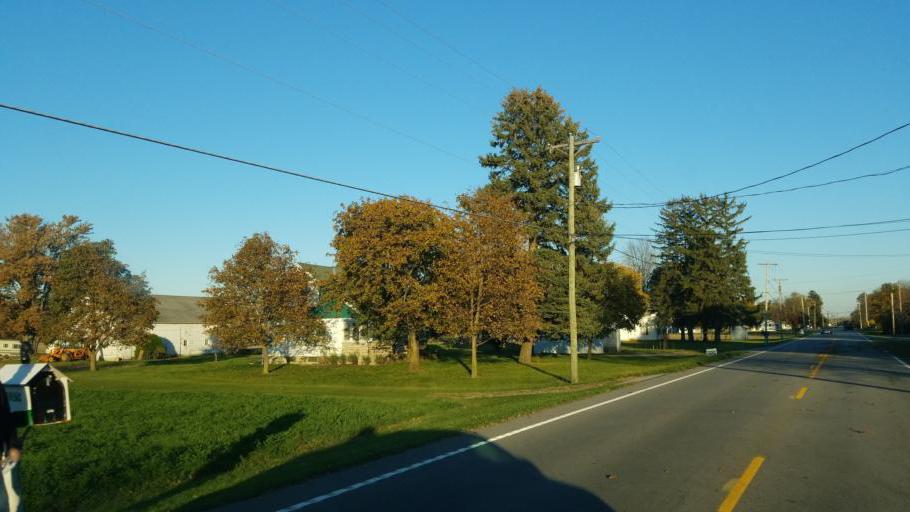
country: US
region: Ohio
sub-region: Sandusky County
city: Clyde
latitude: 41.2924
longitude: -83.0068
